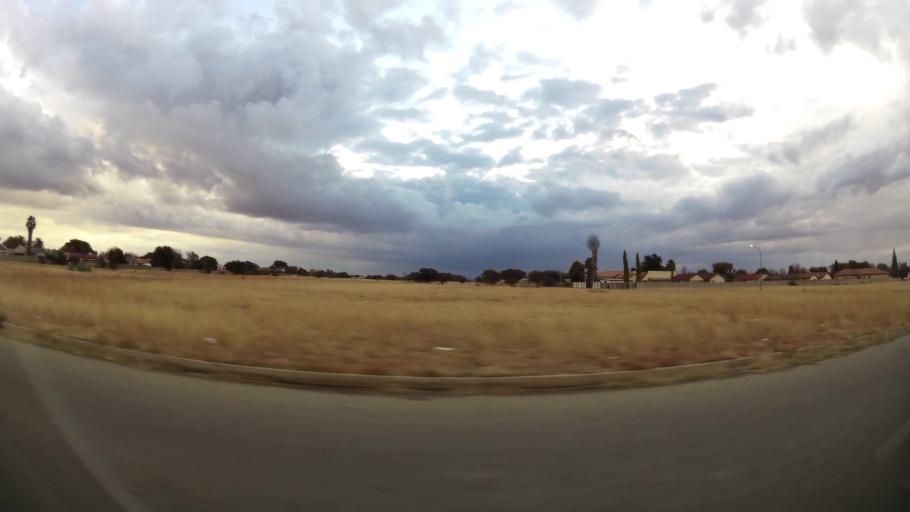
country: ZA
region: Orange Free State
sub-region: Lejweleputswa District Municipality
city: Welkom
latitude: -27.9457
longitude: 26.7349
